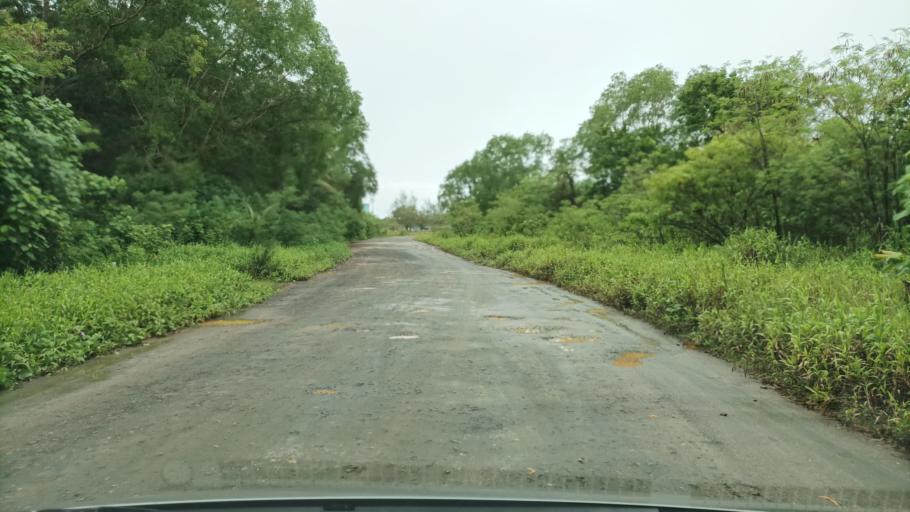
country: FM
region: Yap
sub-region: Weloy Municipality
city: Colonia
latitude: 9.5476
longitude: 138.1631
